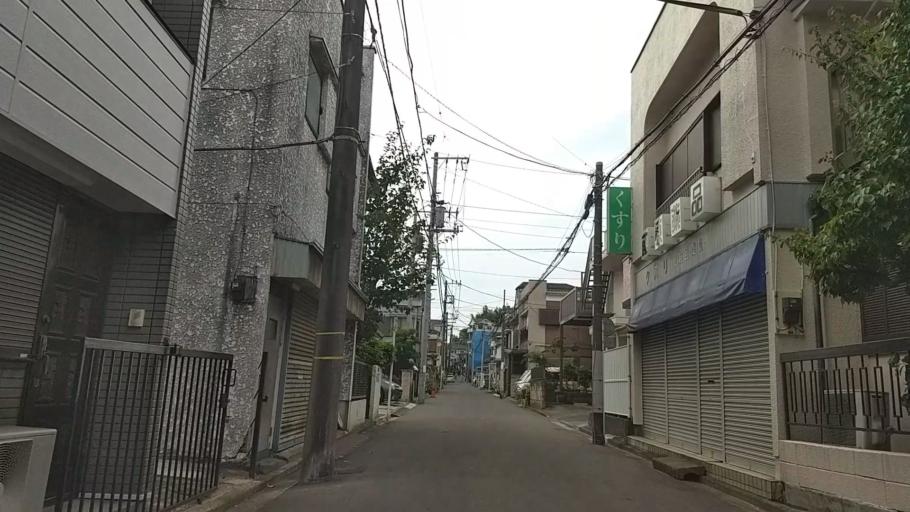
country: JP
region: Kanagawa
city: Yokohama
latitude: 35.4394
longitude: 139.6151
